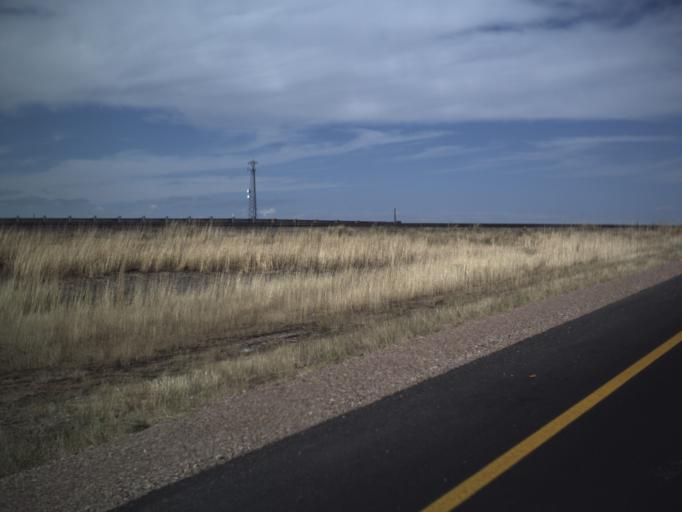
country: US
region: Utah
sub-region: Millard County
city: Fillmore
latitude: 38.8939
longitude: -112.4105
